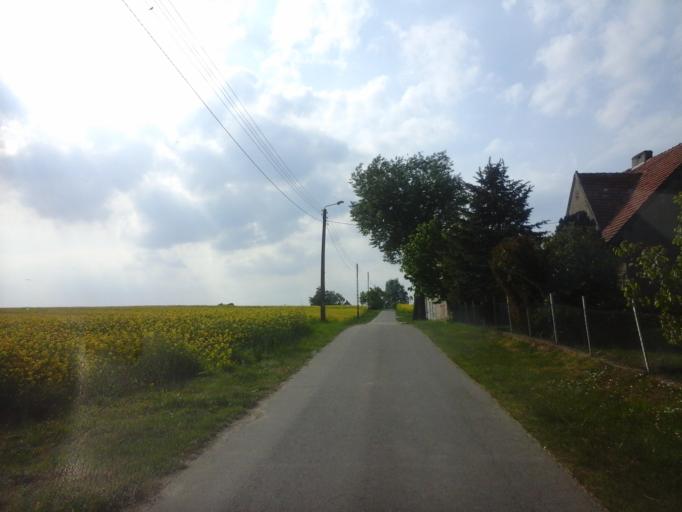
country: PL
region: West Pomeranian Voivodeship
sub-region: Powiat choszczenski
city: Pelczyce
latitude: 53.0313
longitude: 15.2720
